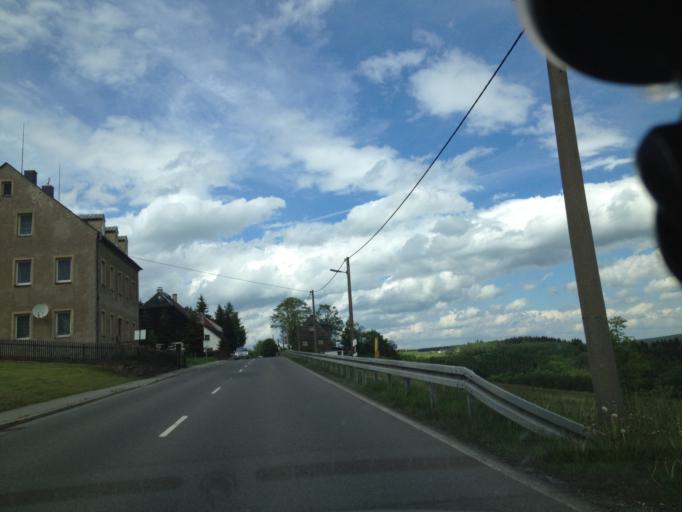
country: DE
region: Saxony
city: Barenstein
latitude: 50.5039
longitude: 13.0271
